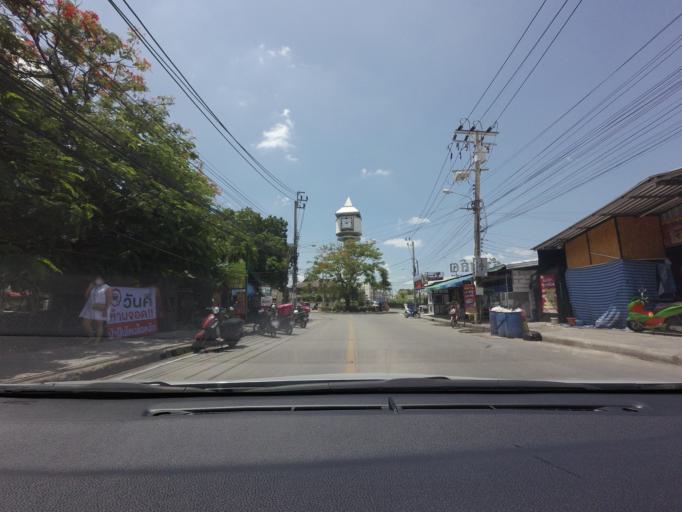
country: TH
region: Bangkok
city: Suan Luang
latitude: 13.7045
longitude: 100.6363
